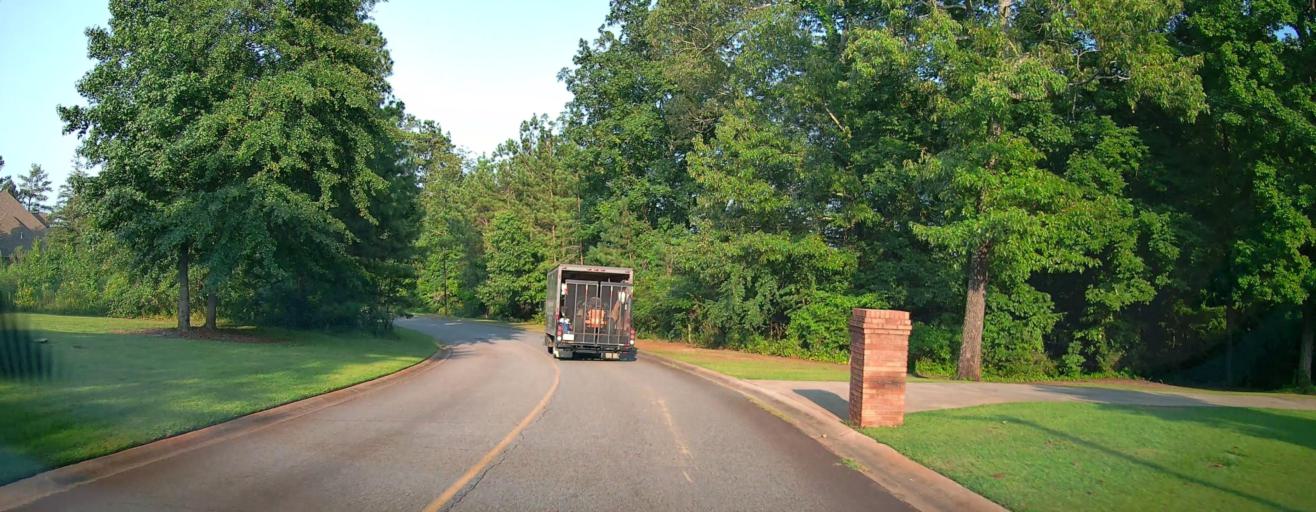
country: US
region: Georgia
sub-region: Bibb County
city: West Point
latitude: 32.8843
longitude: -83.8161
